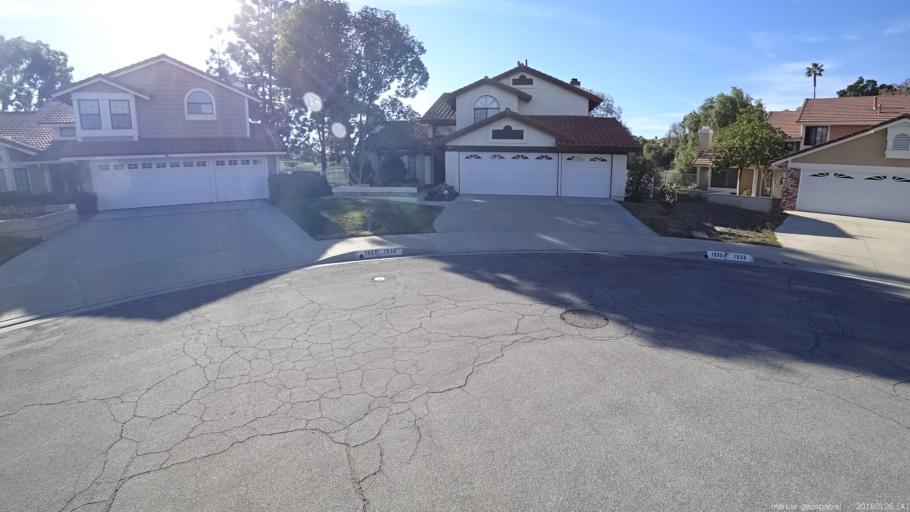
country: US
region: California
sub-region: Los Angeles County
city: Diamond Bar
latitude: 33.9946
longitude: -117.7979
